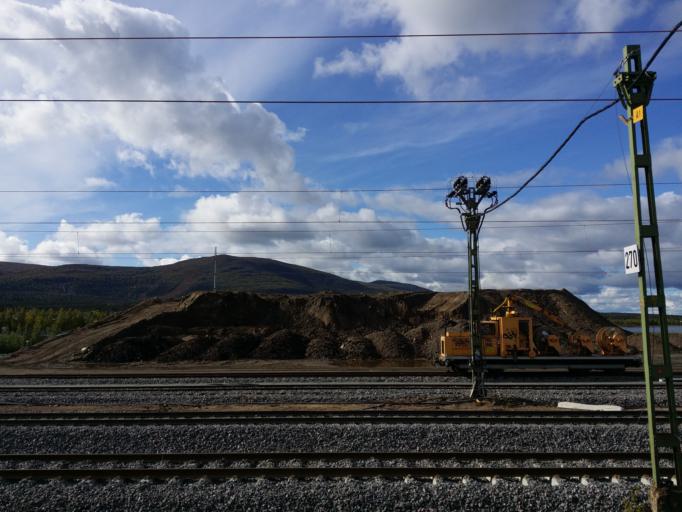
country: SE
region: Norrbotten
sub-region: Gallivare Kommun
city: Gaellivare
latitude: 67.1341
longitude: 20.6496
